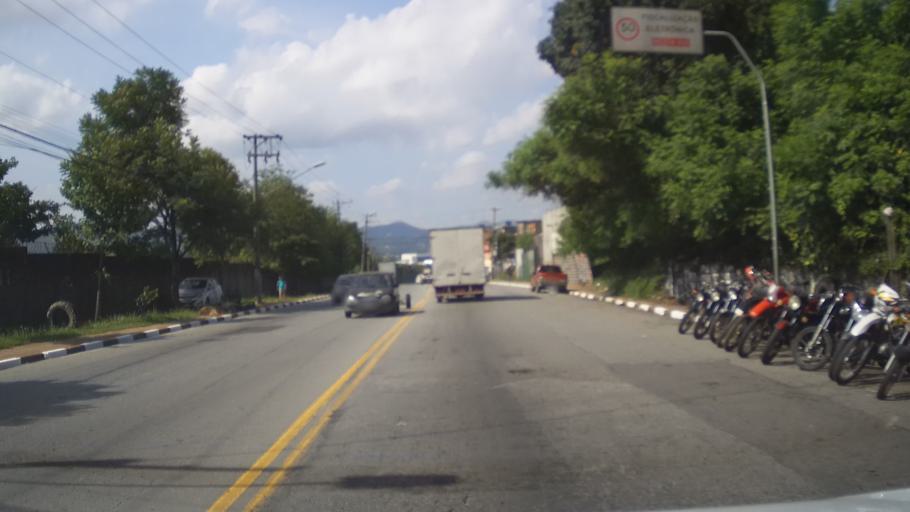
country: BR
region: Sao Paulo
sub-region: Guarulhos
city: Guarulhos
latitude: -23.4405
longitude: -46.4686
